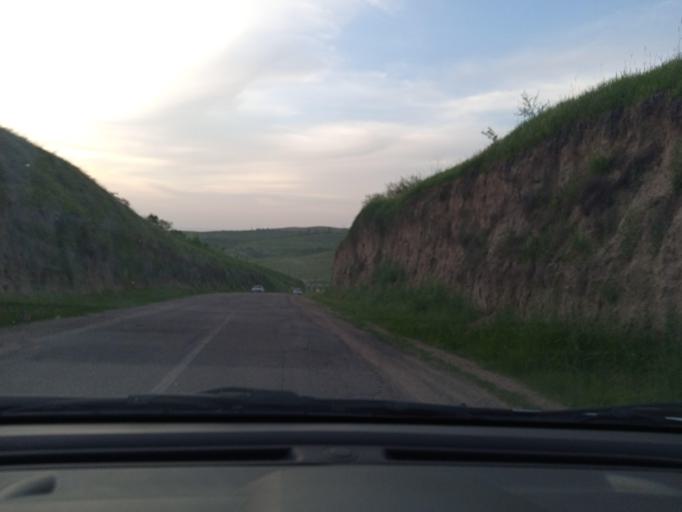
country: UZ
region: Toshkent
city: Parkent
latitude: 41.2386
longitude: 69.7337
